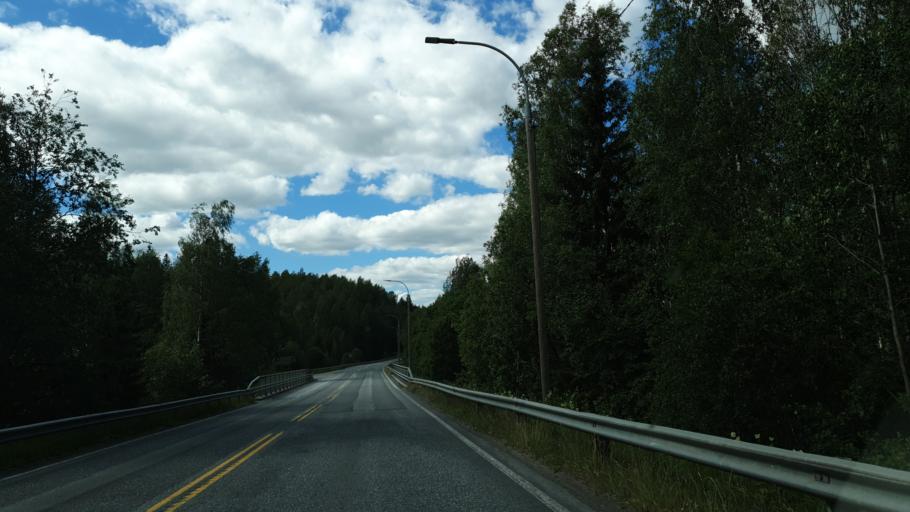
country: FI
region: Northern Savo
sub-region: Kuopio
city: Nilsiae
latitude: 63.1332
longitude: 27.9914
